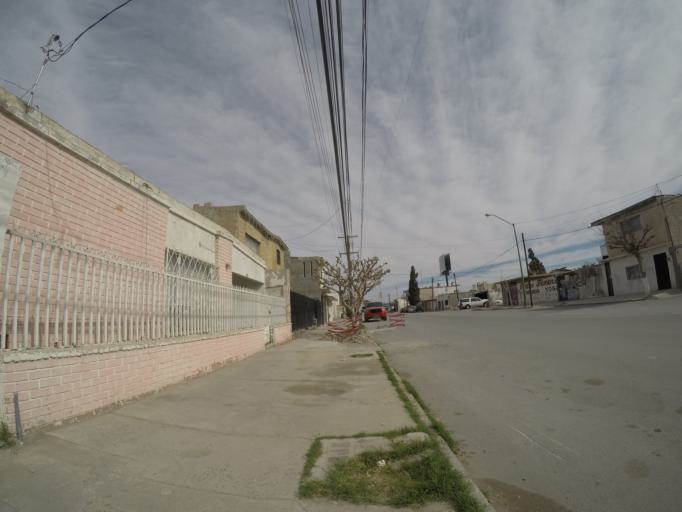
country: MX
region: Chihuahua
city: Ciudad Juarez
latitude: 31.7210
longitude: -106.4262
